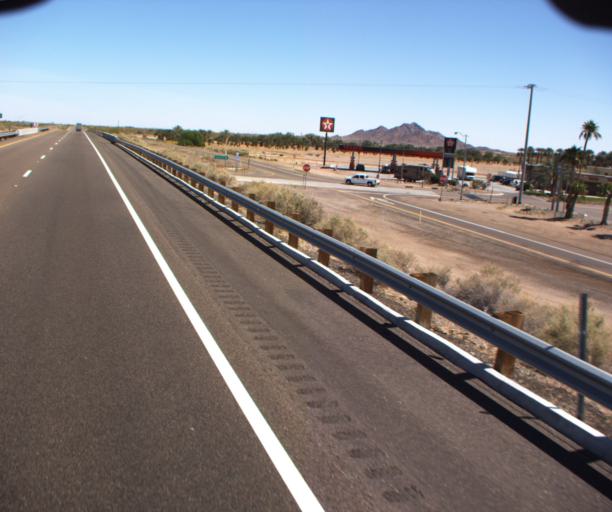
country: US
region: Arizona
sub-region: Yuma County
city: Wellton
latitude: 32.8000
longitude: -113.5420
